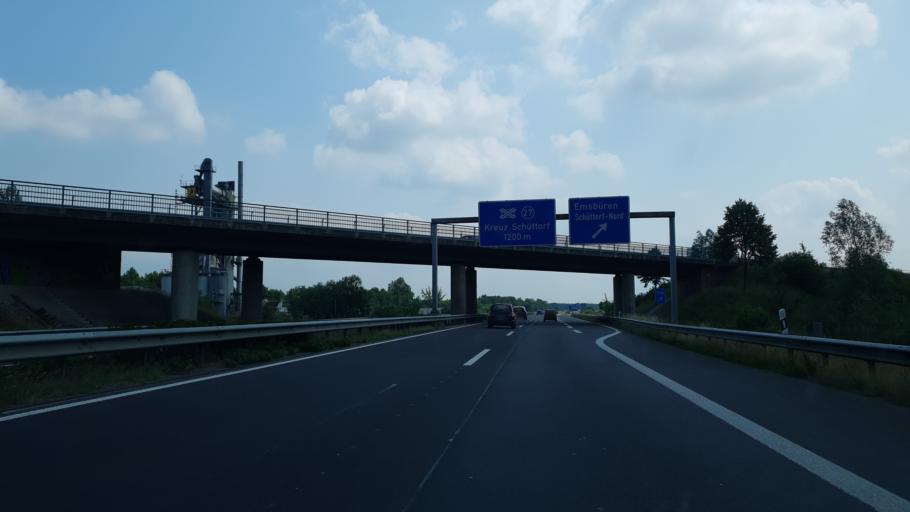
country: DE
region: Lower Saxony
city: Schuttorf
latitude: 52.3574
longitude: 7.2577
